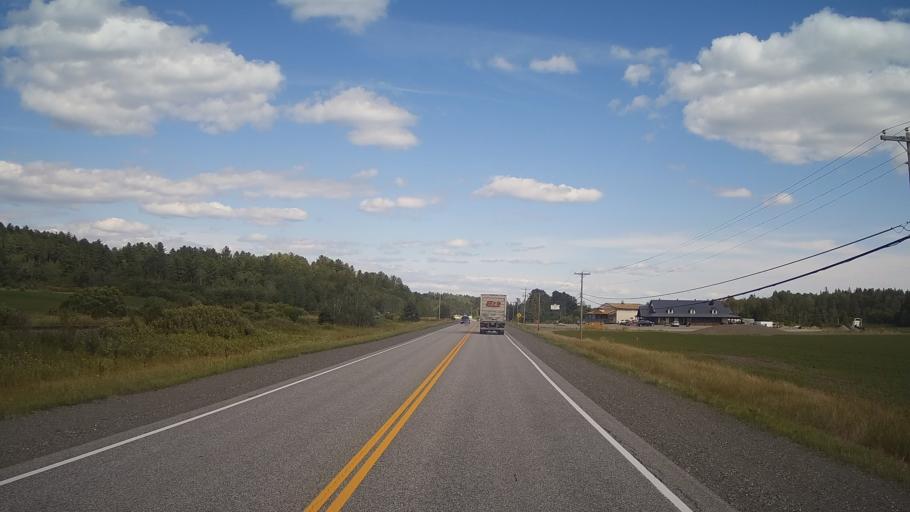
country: CA
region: Ontario
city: Greater Sudbury
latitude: 46.4465
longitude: -80.3595
